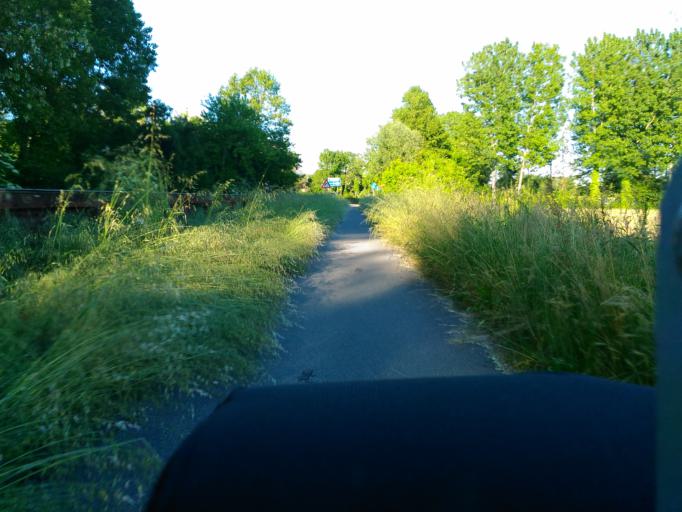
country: IT
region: Lombardy
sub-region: Provincia di Lodi
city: Muzza di Cornegliano Laudense
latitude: 45.3078
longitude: 9.4672
